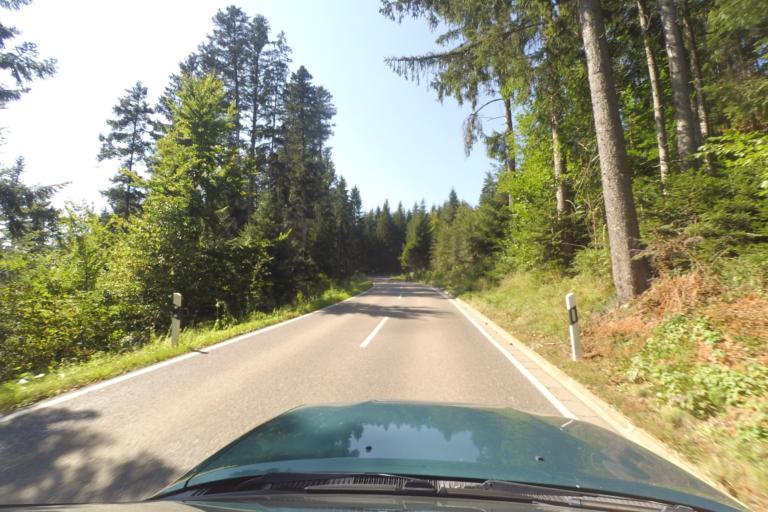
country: DE
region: Baden-Wuerttemberg
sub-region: Regierungsbezirk Stuttgart
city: Taferrot
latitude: 48.8531
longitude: 9.8321
